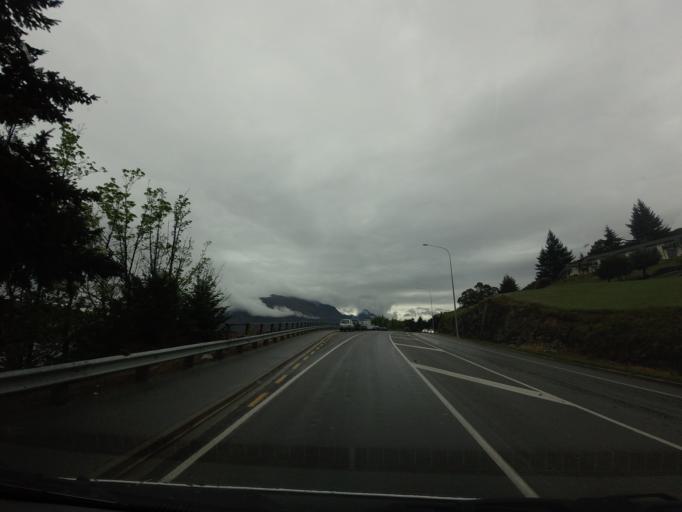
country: NZ
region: Otago
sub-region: Queenstown-Lakes District
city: Queenstown
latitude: -45.0229
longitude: 168.7002
